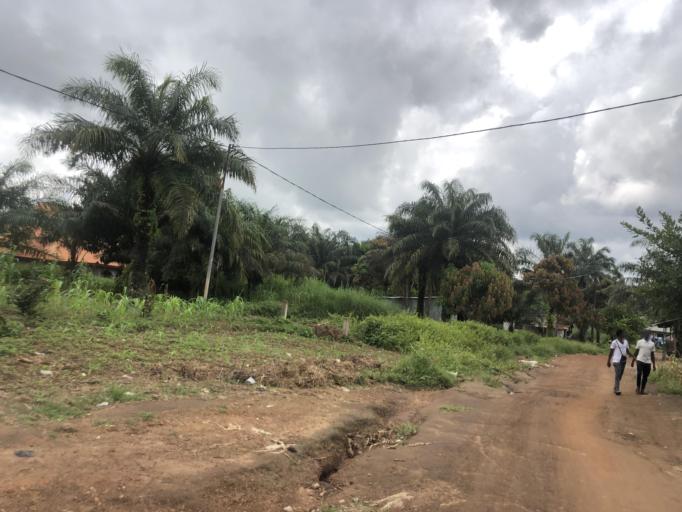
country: SL
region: Northern Province
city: Makeni
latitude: 8.9080
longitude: -12.0396
